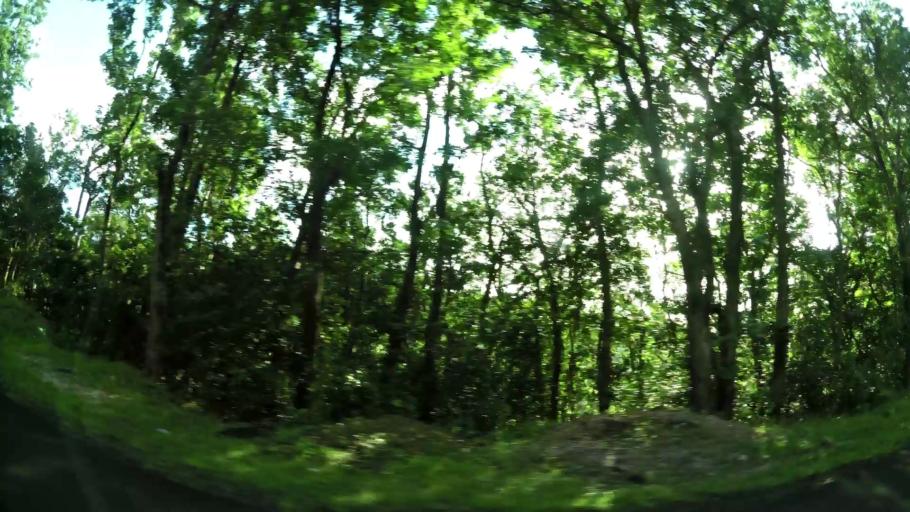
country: GP
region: Guadeloupe
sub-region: Guadeloupe
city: Bouillante
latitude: 16.1820
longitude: -61.7639
